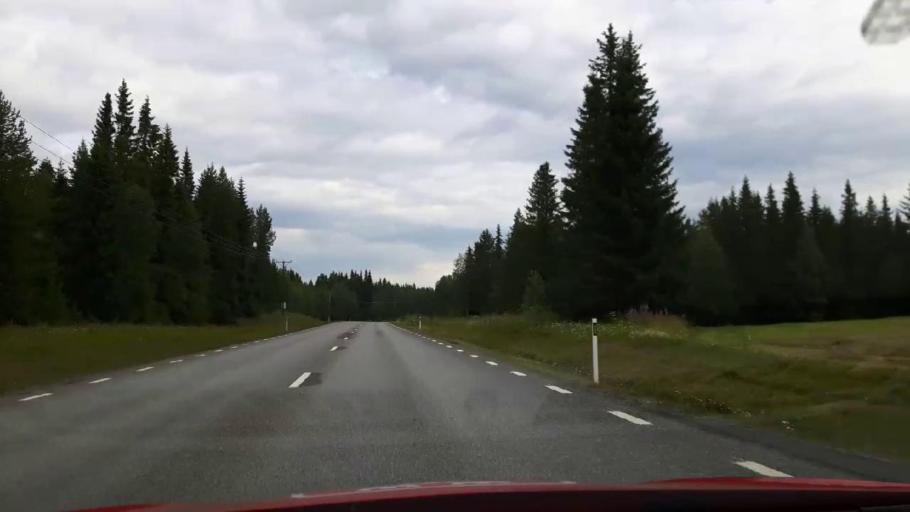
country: SE
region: Jaemtland
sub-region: Stroemsunds Kommun
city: Stroemsund
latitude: 63.6443
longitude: 15.3730
